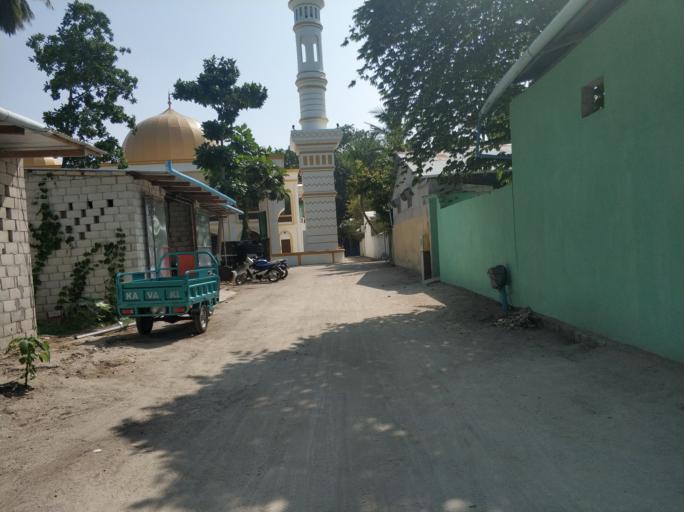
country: MV
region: Maale
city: Male
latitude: 4.4390
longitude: 72.9614
